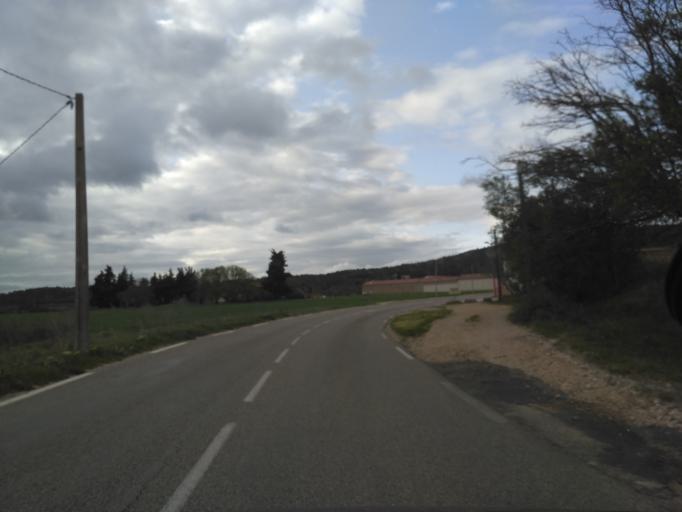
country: FR
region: Provence-Alpes-Cote d'Azur
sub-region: Departement du Var
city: Barjols
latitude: 43.5881
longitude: 6.0132
